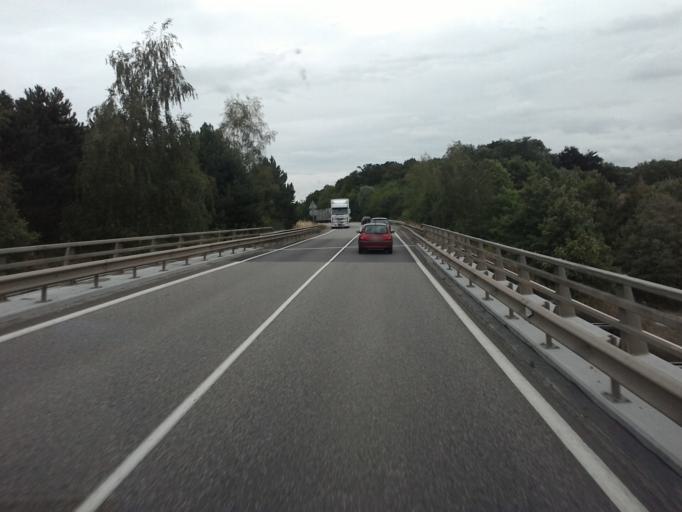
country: FR
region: Lorraine
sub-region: Departement de Meurthe-et-Moselle
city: Mereville
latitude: 48.6036
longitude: 6.1543
